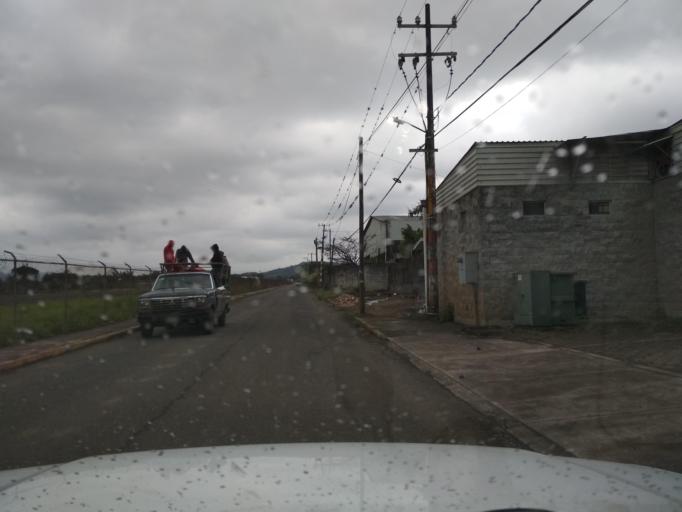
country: MX
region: Veracruz
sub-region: Cordoba
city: Veinte de Noviembre
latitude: 18.8711
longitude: -96.9538
